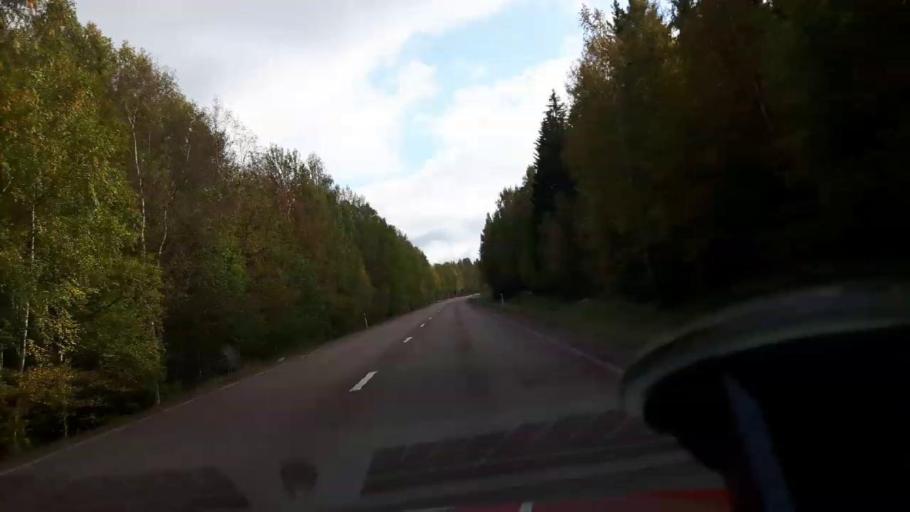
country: SE
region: Gaevleborg
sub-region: Ljusdals Kommun
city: Jaervsoe
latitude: 61.6447
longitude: 16.2145
